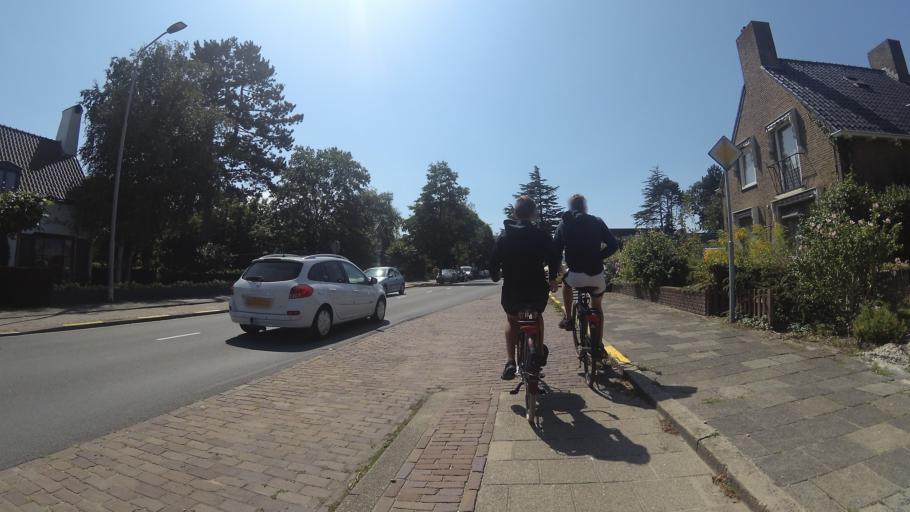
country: NL
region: Zeeland
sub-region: Gemeente Middelburg
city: Middelburg
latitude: 51.4922
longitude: 3.6001
